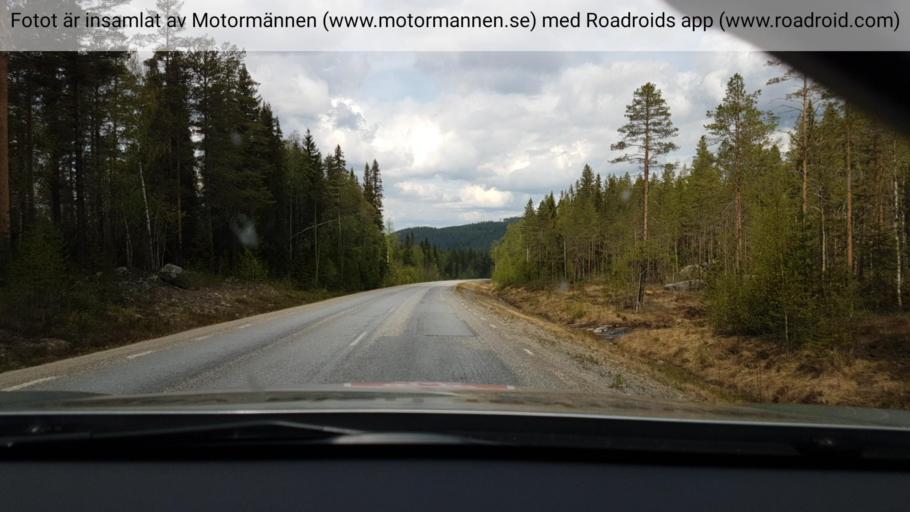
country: SE
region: Vaesternorrland
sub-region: OErnskoeldsviks Kommun
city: Bredbyn
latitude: 63.9201
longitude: 18.4801
